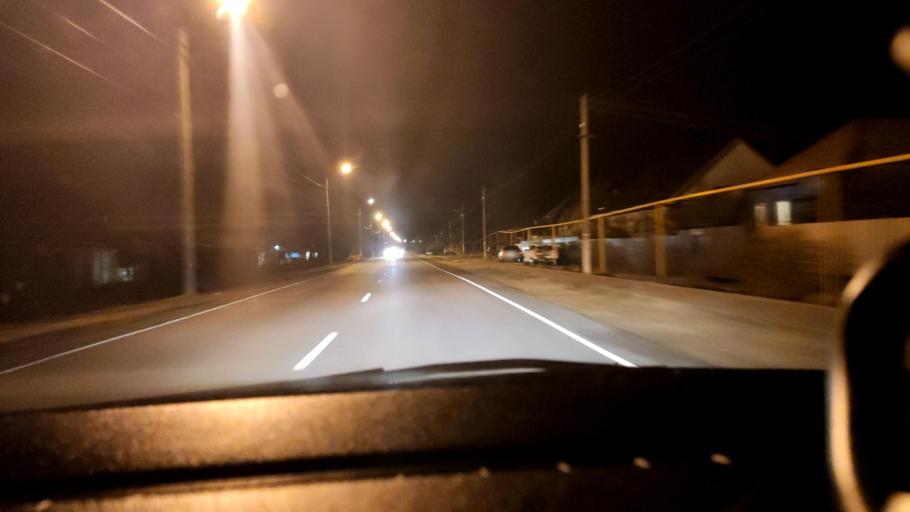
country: RU
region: Voronezj
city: Shilovo
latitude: 51.5631
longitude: 39.0545
